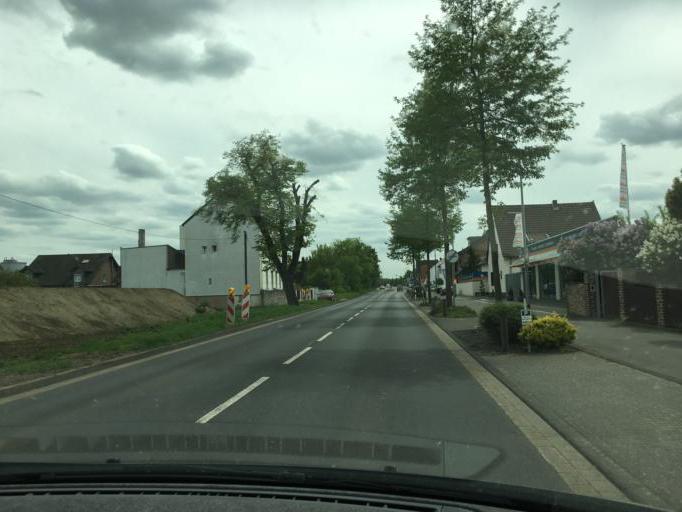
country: DE
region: North Rhine-Westphalia
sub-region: Regierungsbezirk Koln
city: Euskirchen
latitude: 50.6654
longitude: 6.8069
